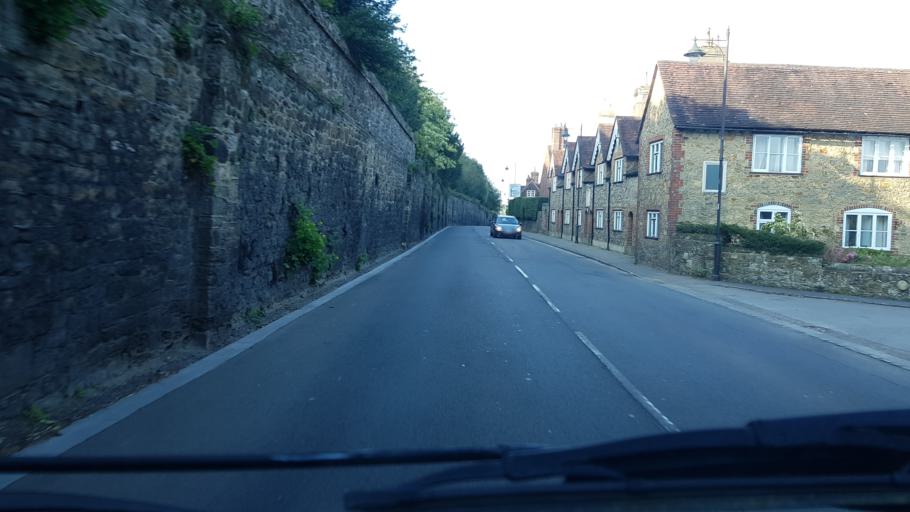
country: GB
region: England
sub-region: West Sussex
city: Petworth
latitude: 50.9903
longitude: -0.6098
